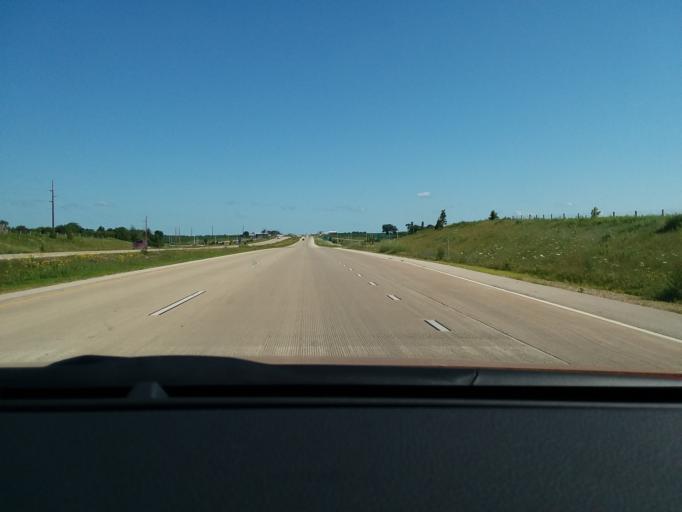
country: US
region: Wisconsin
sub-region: Dane County
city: Windsor
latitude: 43.2105
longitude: -89.3228
